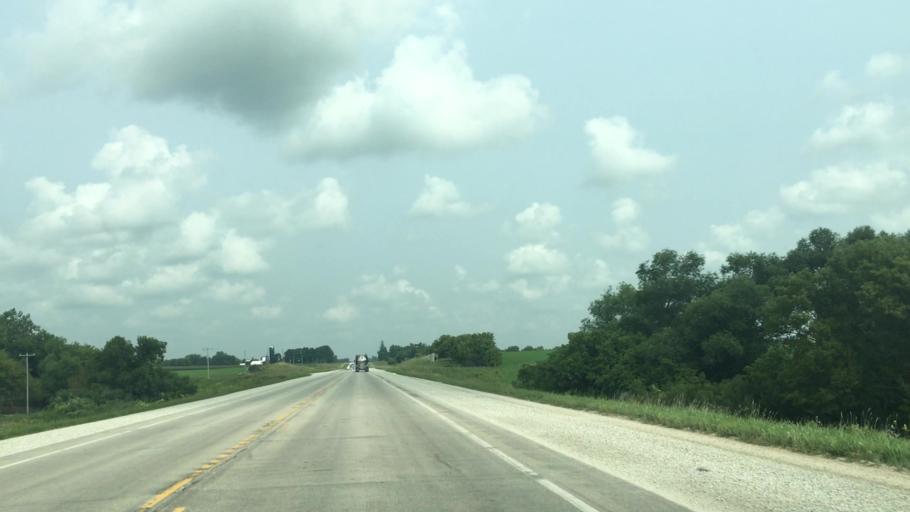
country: US
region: Minnesota
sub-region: Fillmore County
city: Harmony
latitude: 43.4629
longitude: -91.8697
